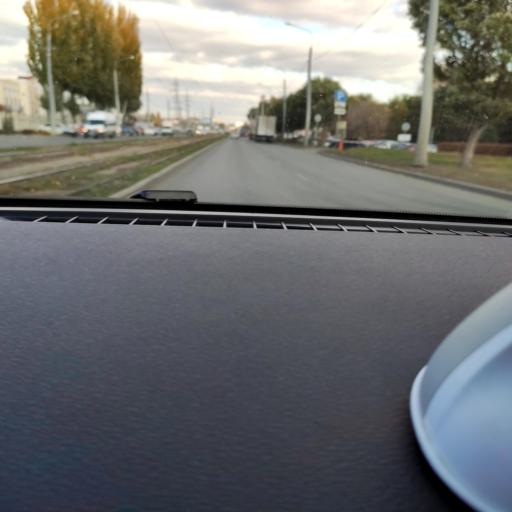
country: RU
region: Samara
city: Samara
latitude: 53.2005
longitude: 50.2594
